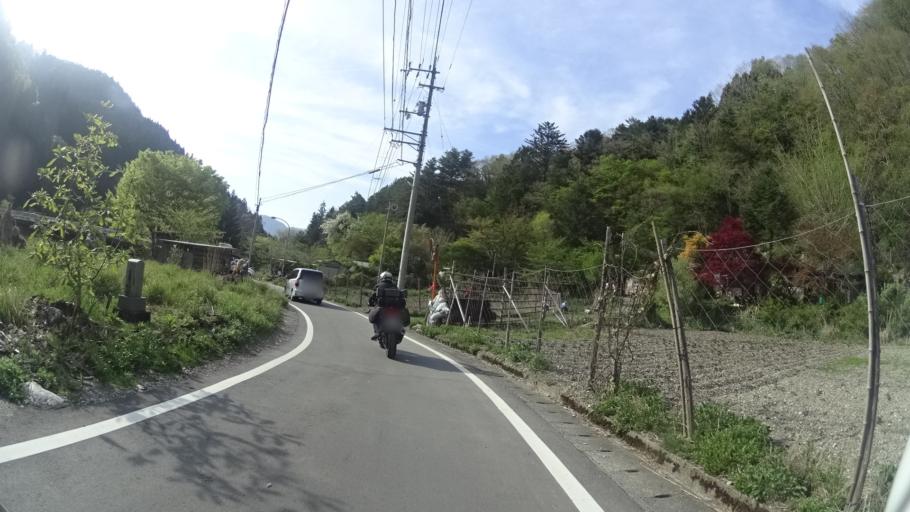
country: JP
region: Tokushima
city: Wakimachi
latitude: 33.8562
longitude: 134.0199
